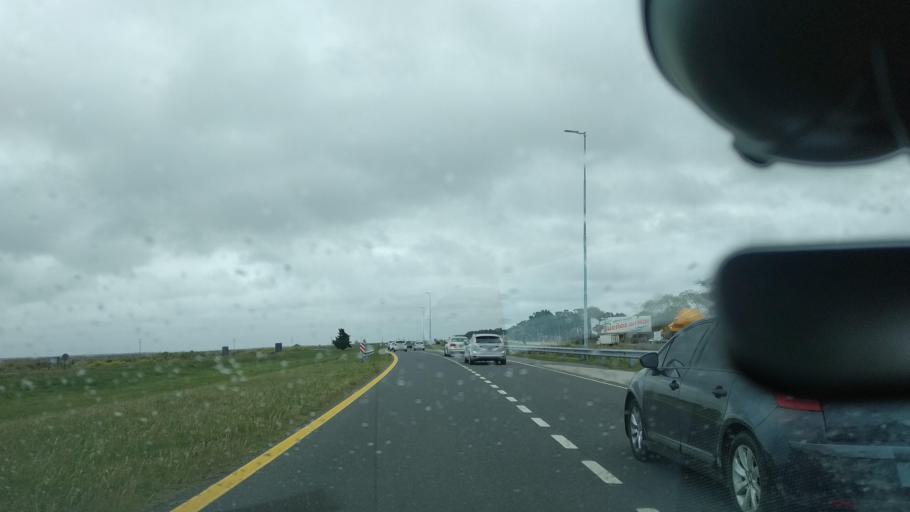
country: AR
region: Buenos Aires
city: San Clemente del Tuyu
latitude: -36.3891
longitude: -56.7433
